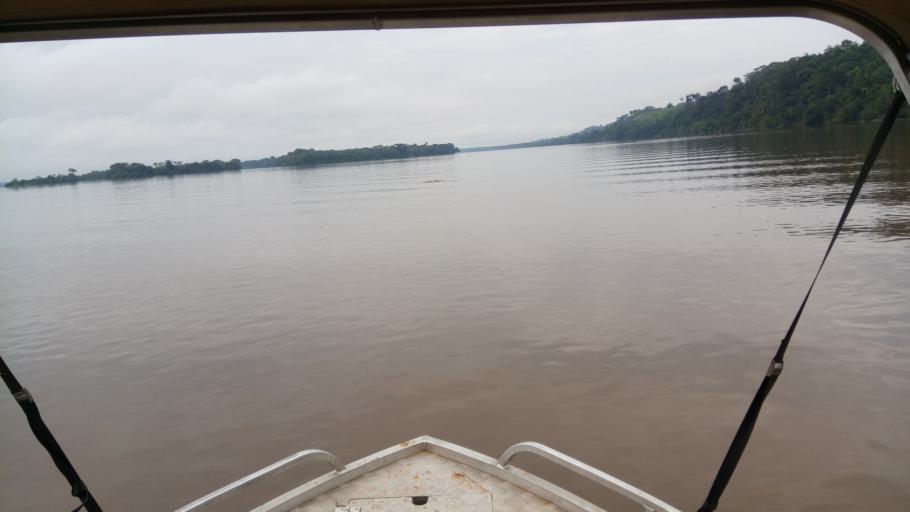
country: CD
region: Eastern Province
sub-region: Sous-Region de la Tshopo
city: Yangambi
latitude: 0.7556
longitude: 24.4820
